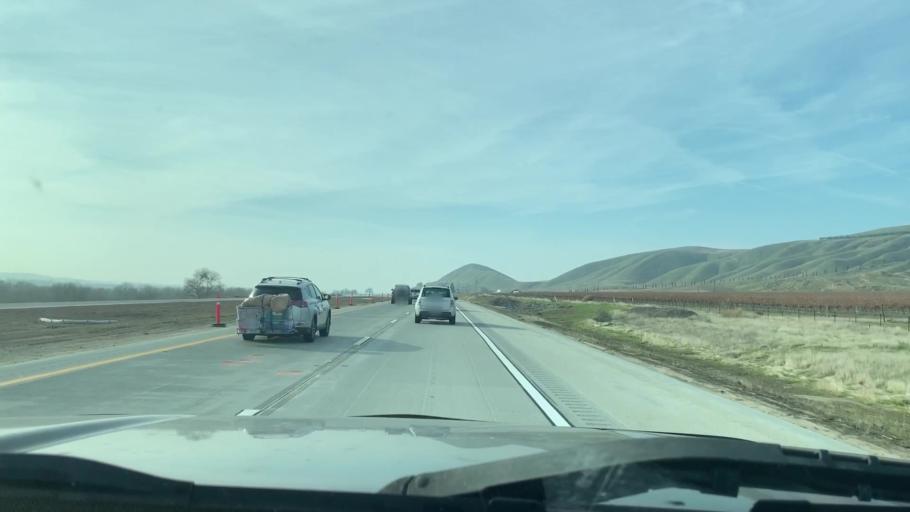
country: US
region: California
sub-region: San Luis Obispo County
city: Shandon
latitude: 35.6623
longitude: -120.3901
